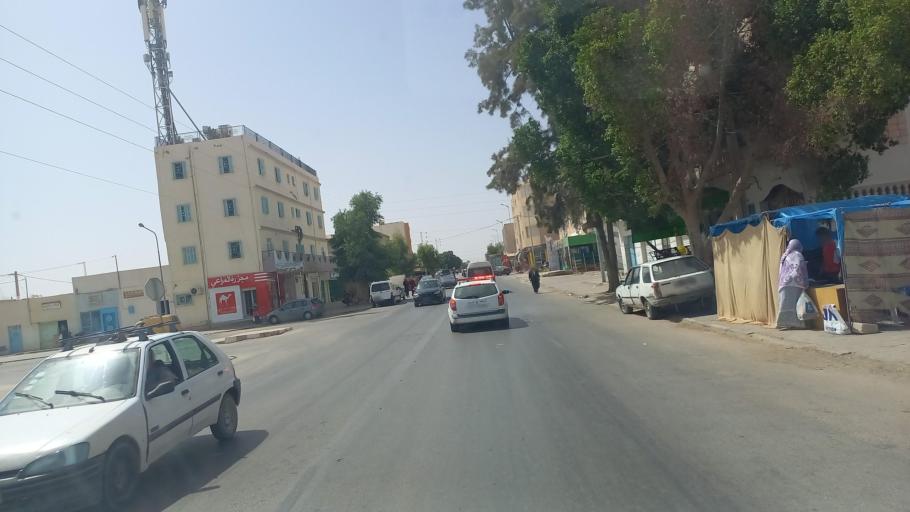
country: TN
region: Madanin
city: Medenine
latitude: 33.3291
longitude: 10.4850
